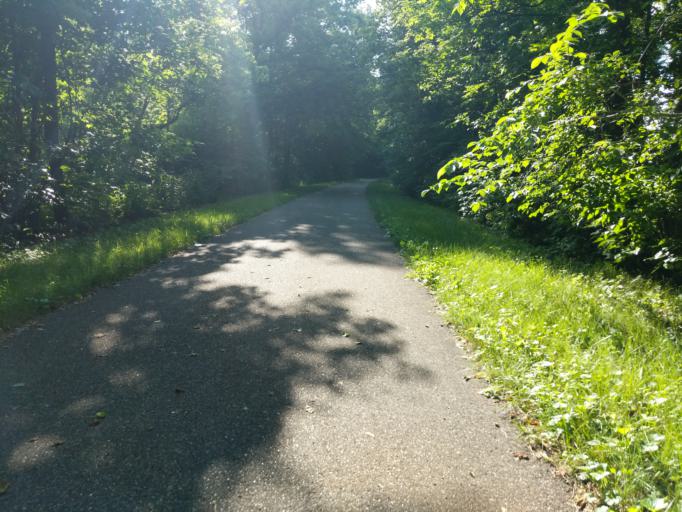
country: US
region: Ohio
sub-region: Athens County
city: Nelsonville
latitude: 39.4281
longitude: -82.2020
